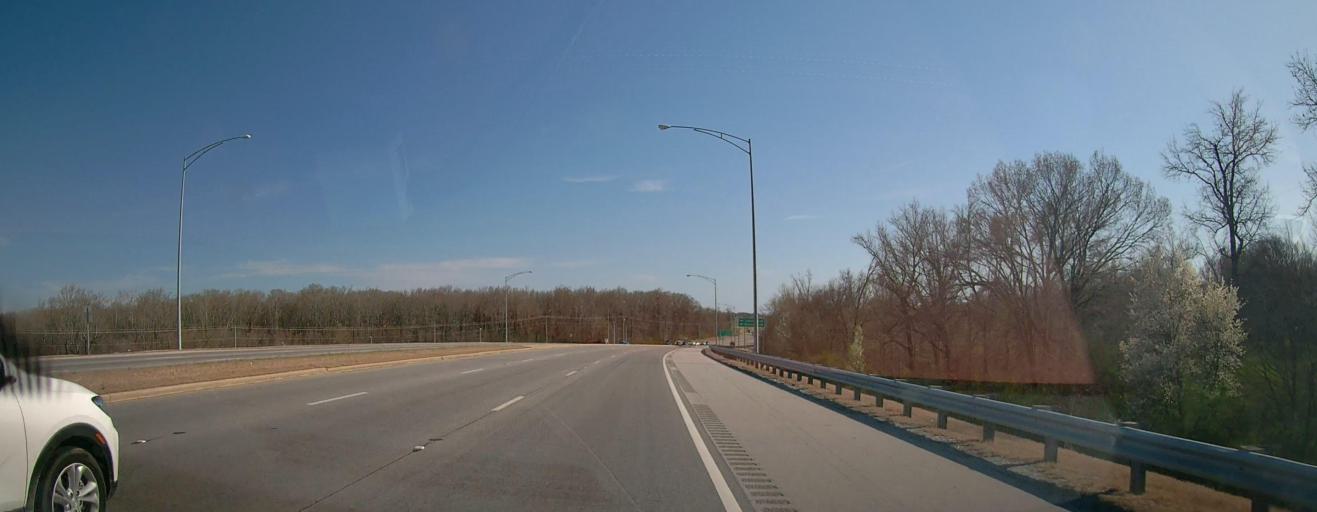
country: US
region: Alabama
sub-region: Lauderdale County
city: East Florence
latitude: 34.7810
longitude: -87.6348
